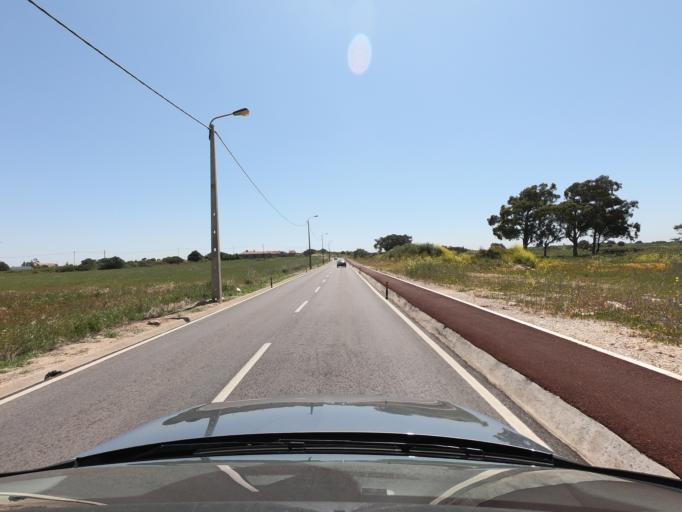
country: PT
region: Lisbon
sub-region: Cascais
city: Sao Domingos de Rana
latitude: 38.7342
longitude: -9.3519
